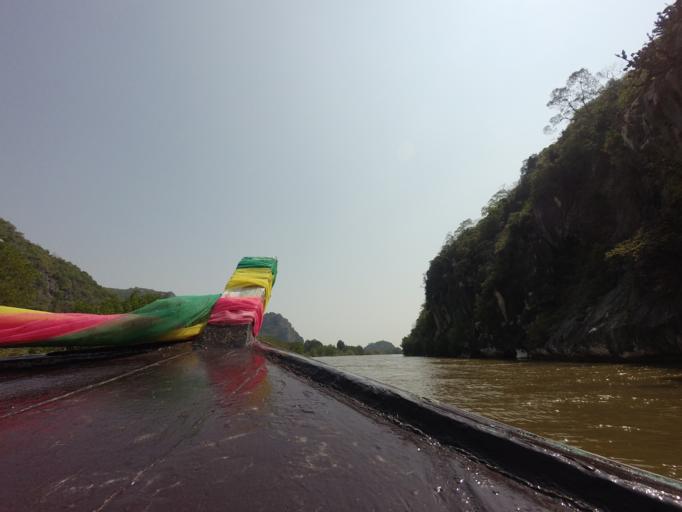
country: TH
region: Prachuap Khiri Khan
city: Kui Buri
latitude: 12.1424
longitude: 99.9526
